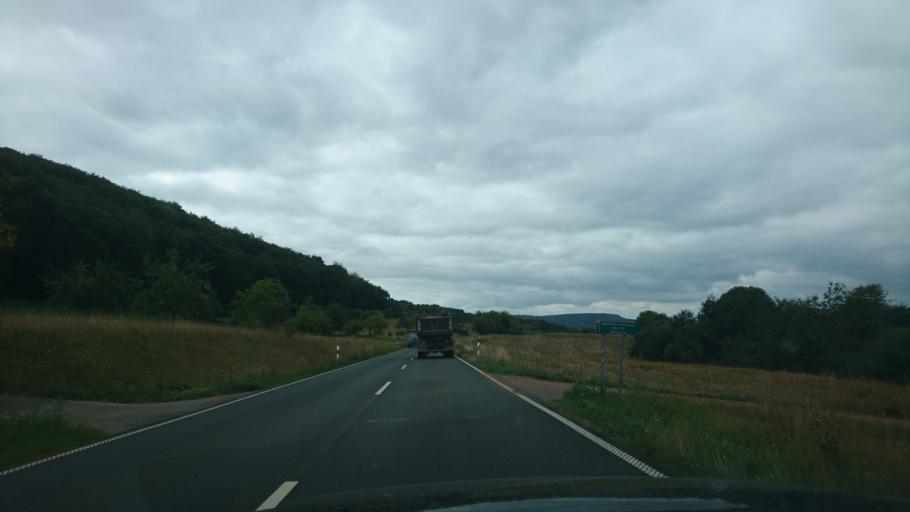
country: DE
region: Rheinland-Pfalz
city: Wiltingen
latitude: 49.6897
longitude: 6.6003
